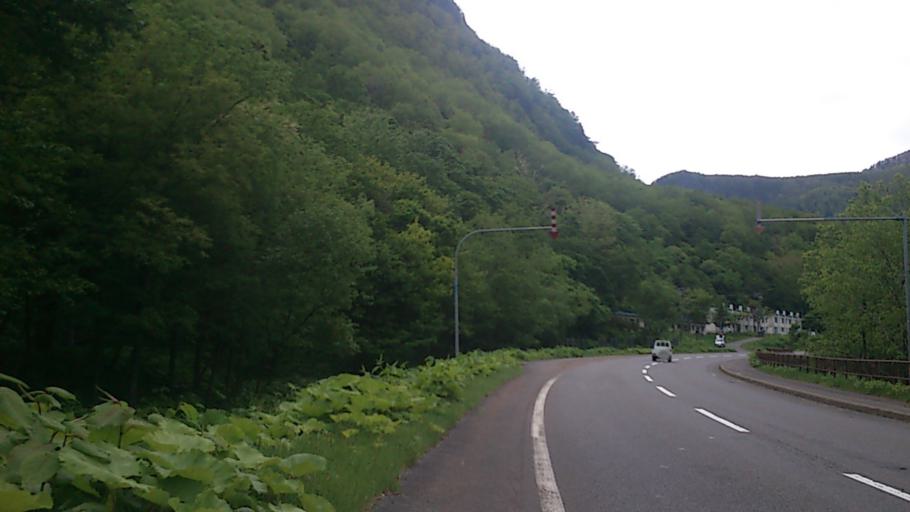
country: JP
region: Hokkaido
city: Kamikawa
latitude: 43.7350
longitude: 142.9425
